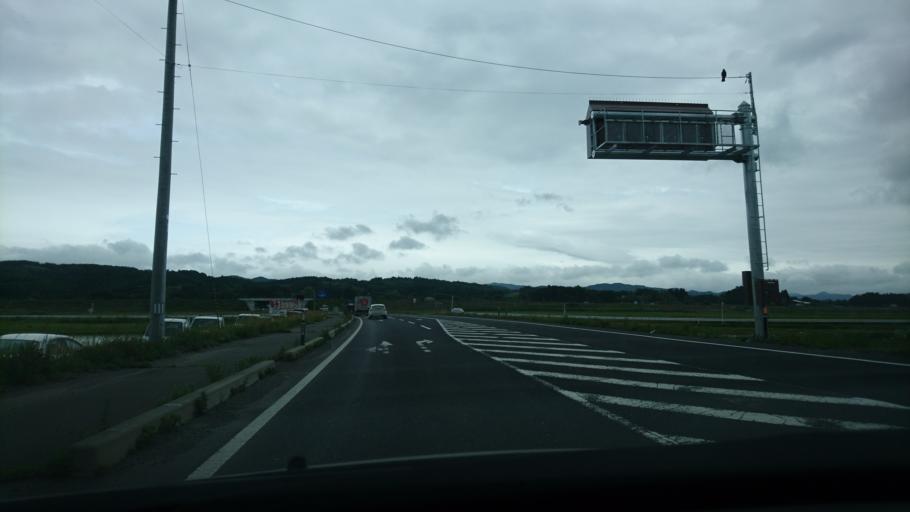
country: JP
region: Miyagi
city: Wakuya
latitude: 38.6773
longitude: 141.2615
